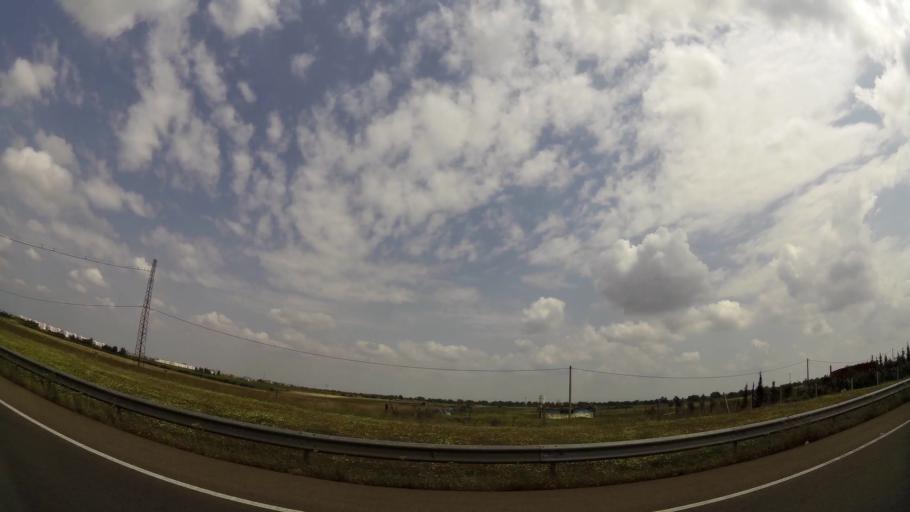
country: MA
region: Rabat-Sale-Zemmour-Zaer
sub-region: Khemisset
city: Tiflet
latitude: 33.9798
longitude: -6.5225
